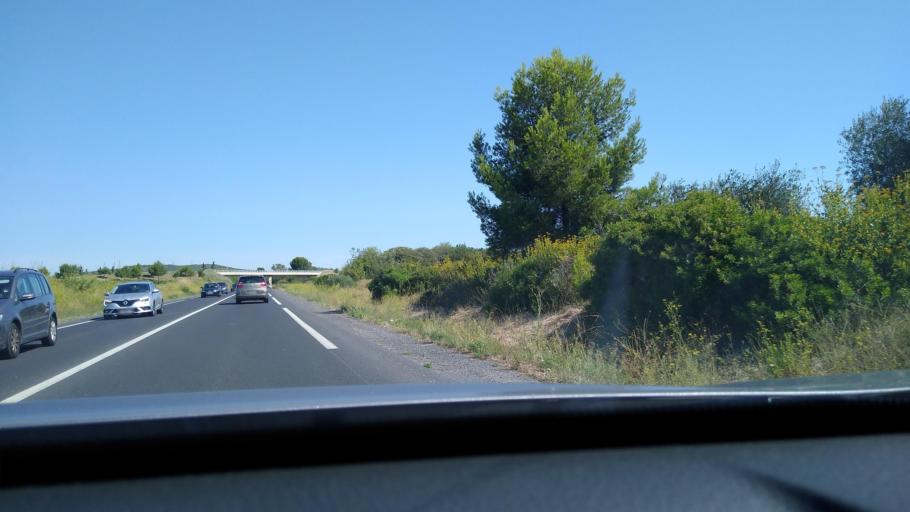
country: FR
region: Languedoc-Roussillon
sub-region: Departement de l'Herault
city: Sete
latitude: 43.4273
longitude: 3.7221
